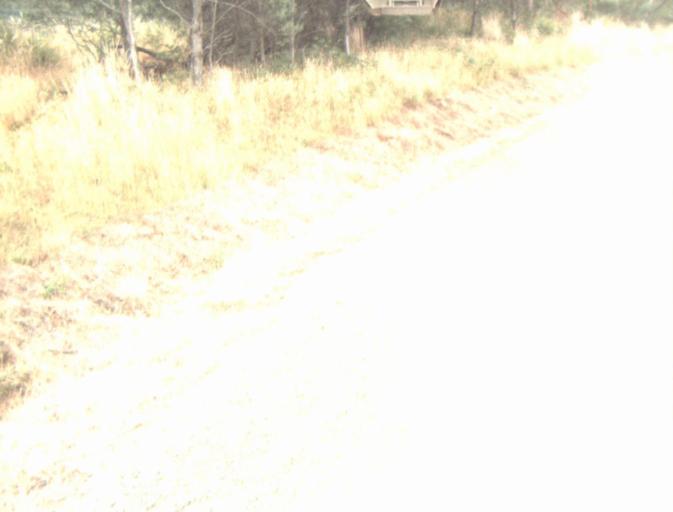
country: AU
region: Tasmania
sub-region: Northern Midlands
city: Evandale
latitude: -41.4591
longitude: 147.4593
